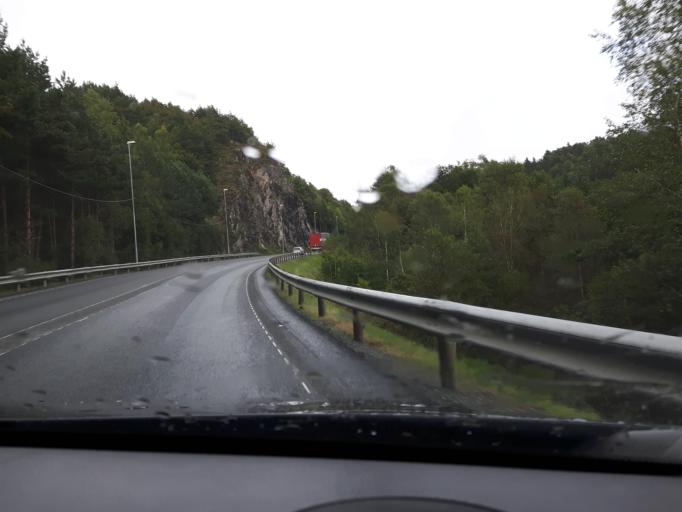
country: NO
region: Vest-Agder
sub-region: Marnardal
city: Helland
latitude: 58.0959
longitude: 7.6322
